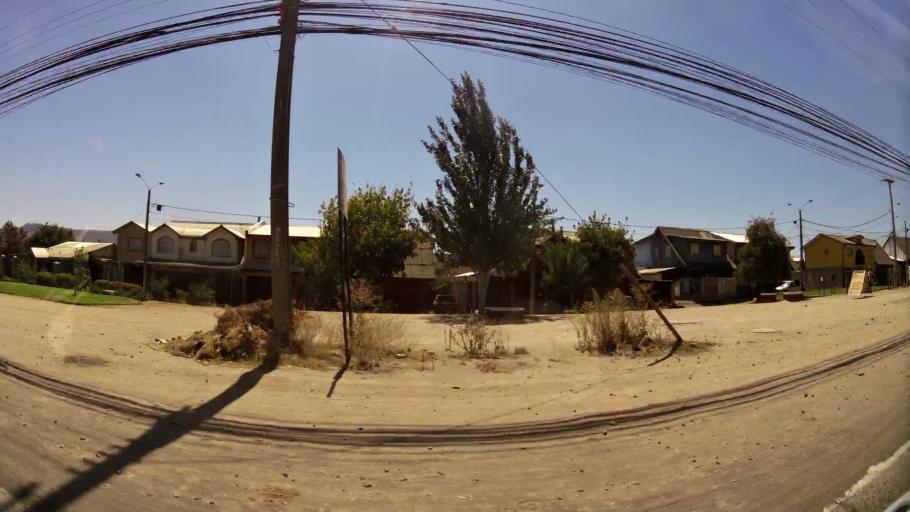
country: CL
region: Maule
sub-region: Provincia de Talca
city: Talca
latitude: -35.4077
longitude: -71.6467
